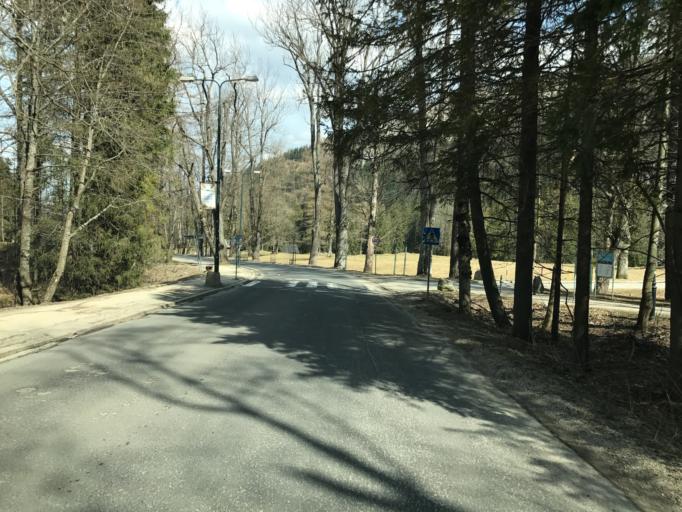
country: PL
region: Lesser Poland Voivodeship
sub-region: Powiat tatrzanski
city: Zakopane
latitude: 49.2724
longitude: 19.9808
